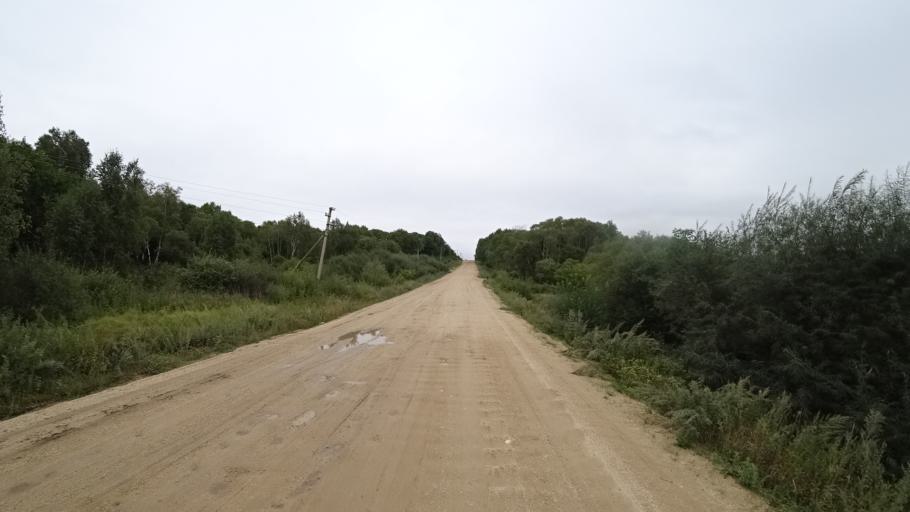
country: RU
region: Primorskiy
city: Ivanovka
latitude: 44.0727
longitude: 132.5827
